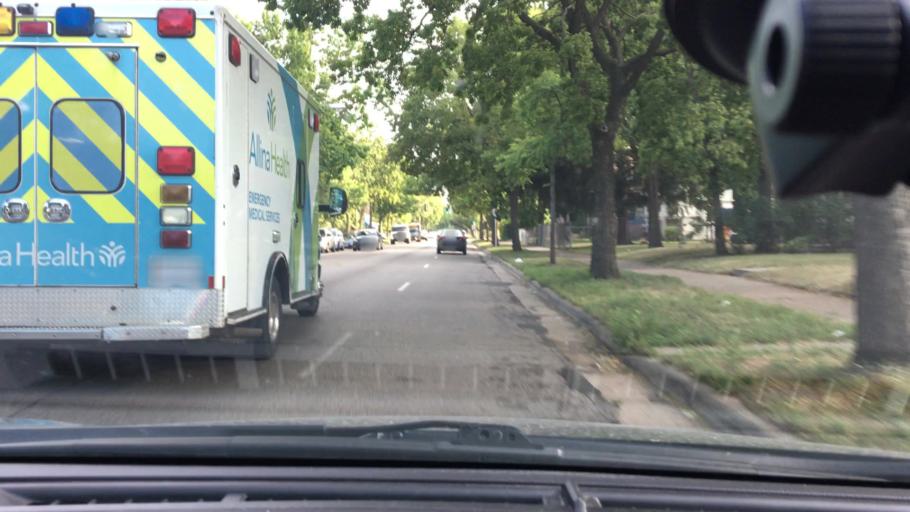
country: US
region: Minnesota
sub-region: Hennepin County
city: Minneapolis
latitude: 44.9463
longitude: -93.2475
